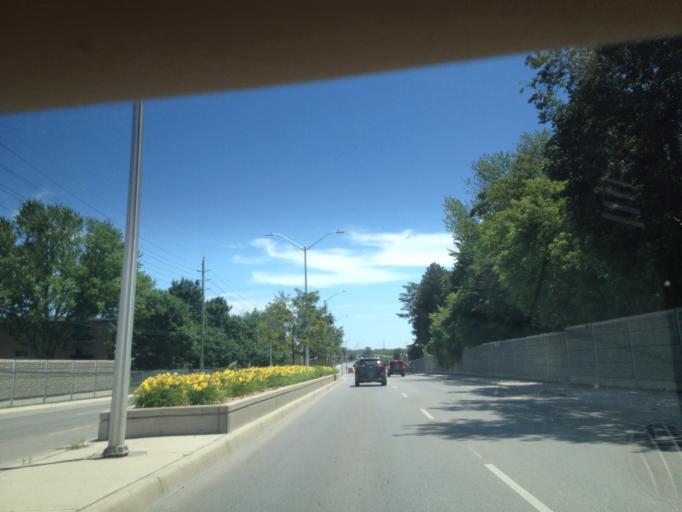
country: CA
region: Ontario
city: London
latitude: 42.9803
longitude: -81.3228
